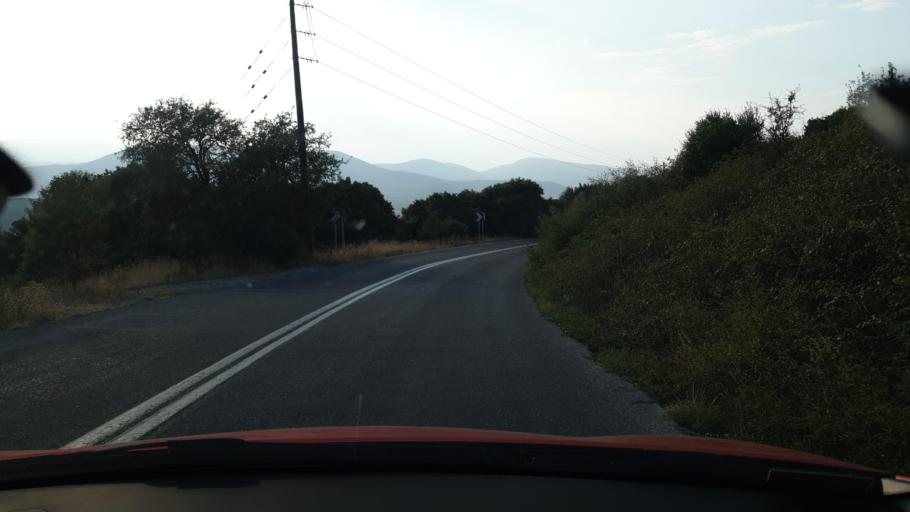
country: GR
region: Thessaly
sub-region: Nomos Magnisias
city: Pteleos
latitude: 39.0667
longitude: 22.9230
